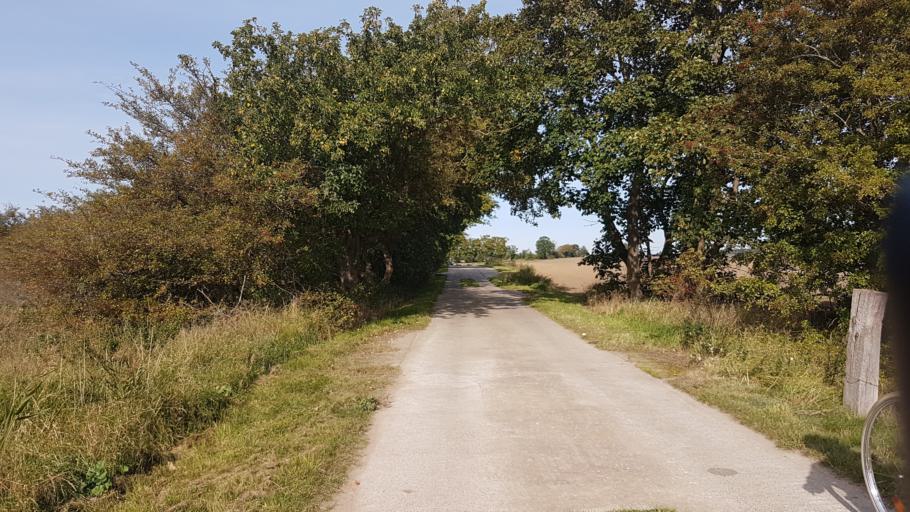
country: DE
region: Mecklenburg-Vorpommern
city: Gingst
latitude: 54.4064
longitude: 13.2563
